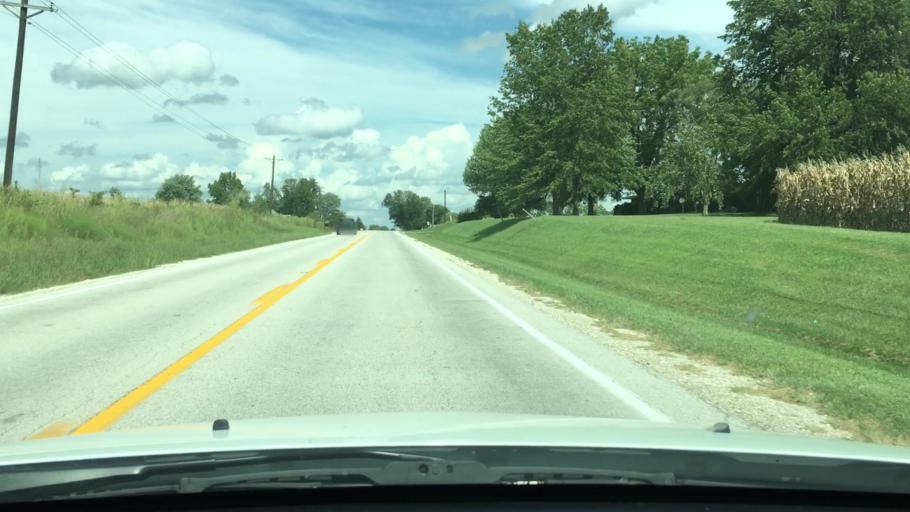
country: US
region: Illinois
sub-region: Pike County
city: Pittsfield
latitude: 39.5526
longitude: -90.9165
